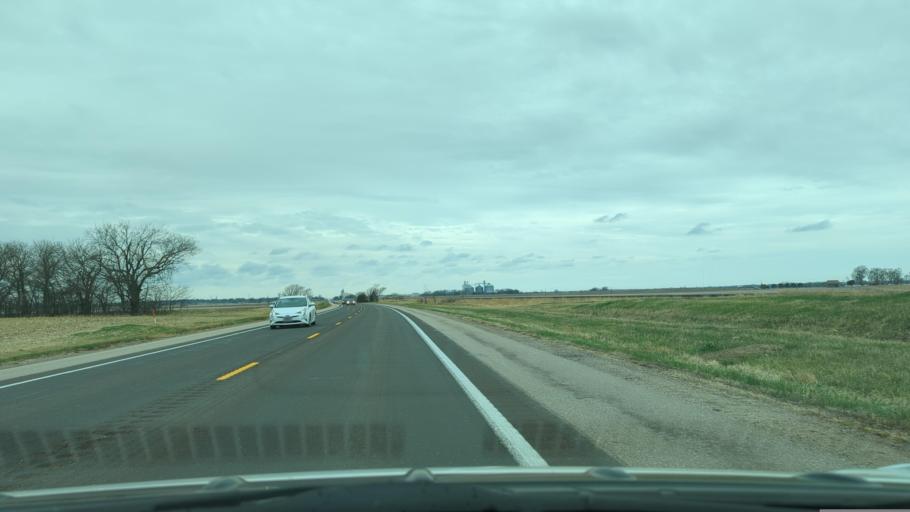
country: US
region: Nebraska
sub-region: Lancaster County
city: Waverly
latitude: 40.9358
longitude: -96.4910
